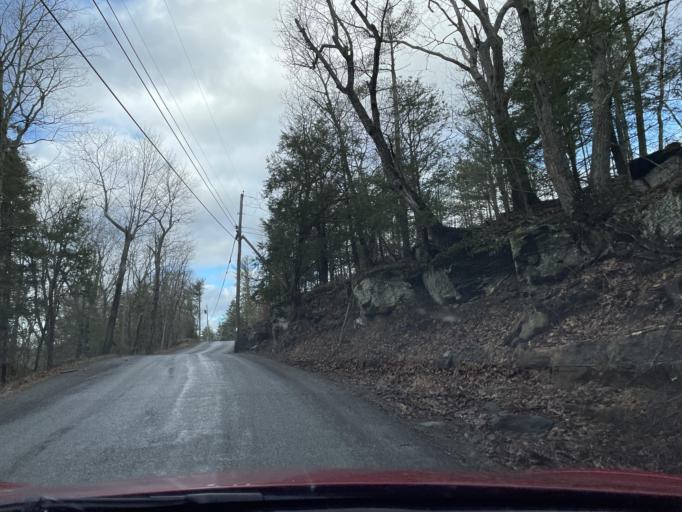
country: US
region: New York
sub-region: Ulster County
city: Manorville
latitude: 42.0843
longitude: -74.0458
